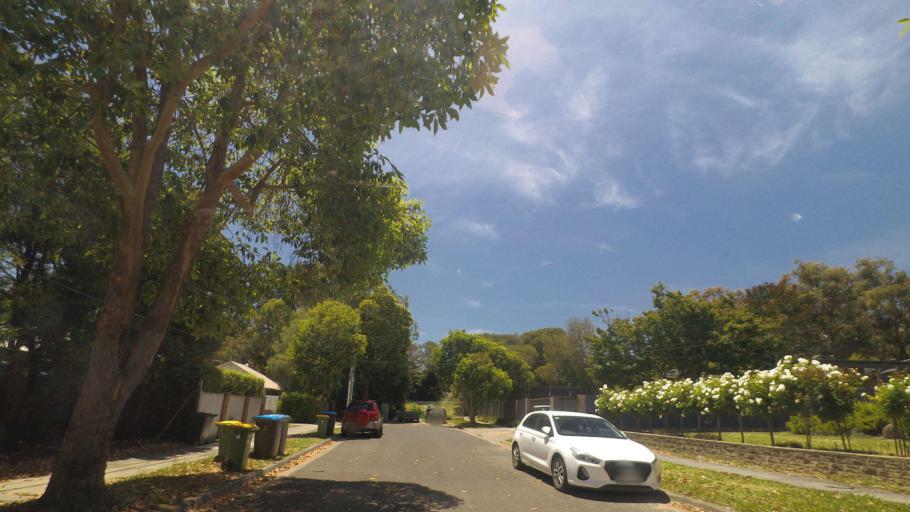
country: AU
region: Victoria
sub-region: Knox
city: Boronia
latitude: -37.8595
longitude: 145.2984
